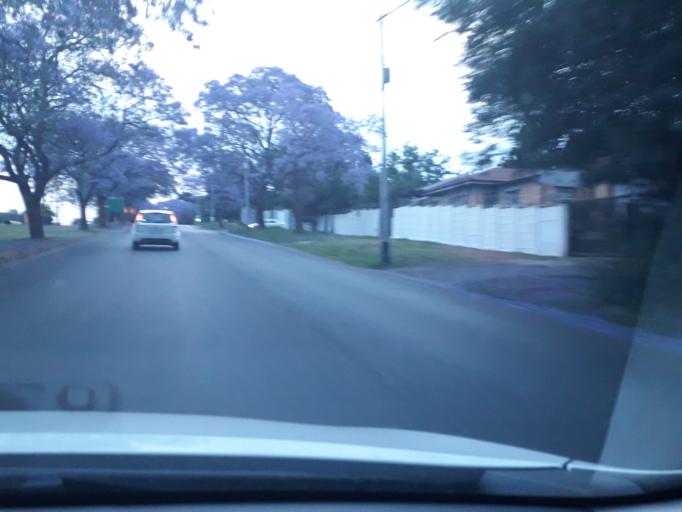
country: ZA
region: Gauteng
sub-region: City of Johannesburg Metropolitan Municipality
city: Johannesburg
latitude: -26.1502
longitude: 27.9902
